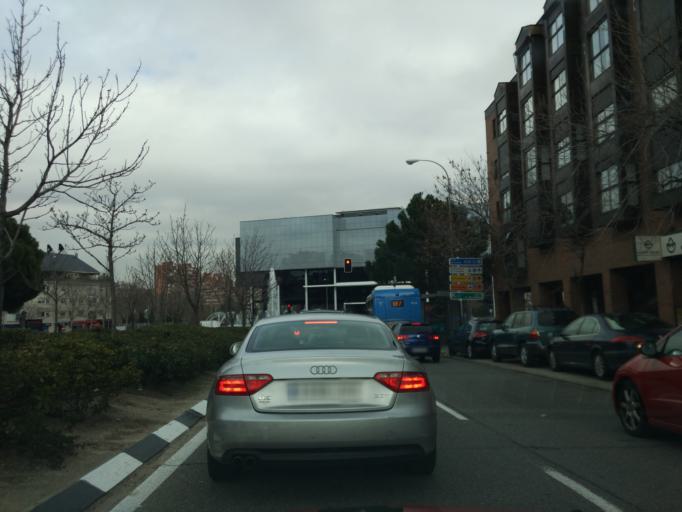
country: ES
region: Madrid
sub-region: Provincia de Madrid
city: Hortaleza
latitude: 40.4692
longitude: -3.6436
